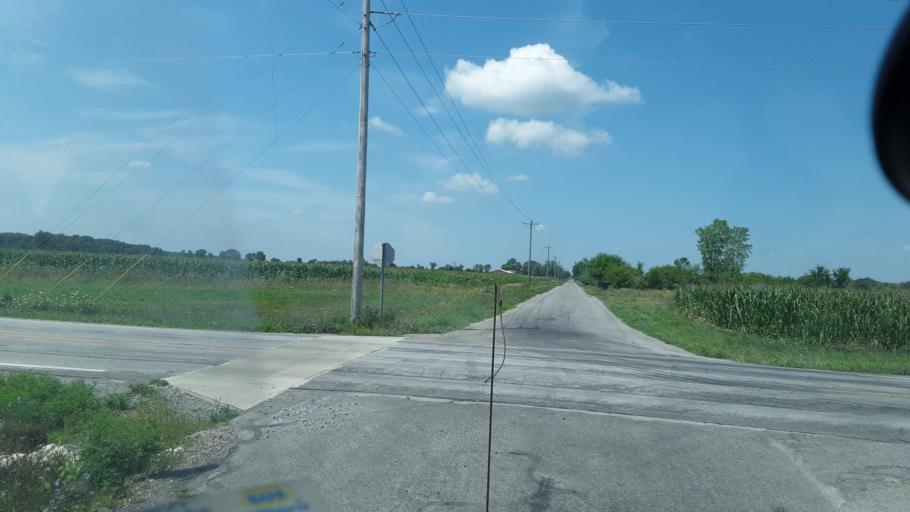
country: US
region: Ohio
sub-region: Hancock County
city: Findlay
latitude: 40.9716
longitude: -83.5743
